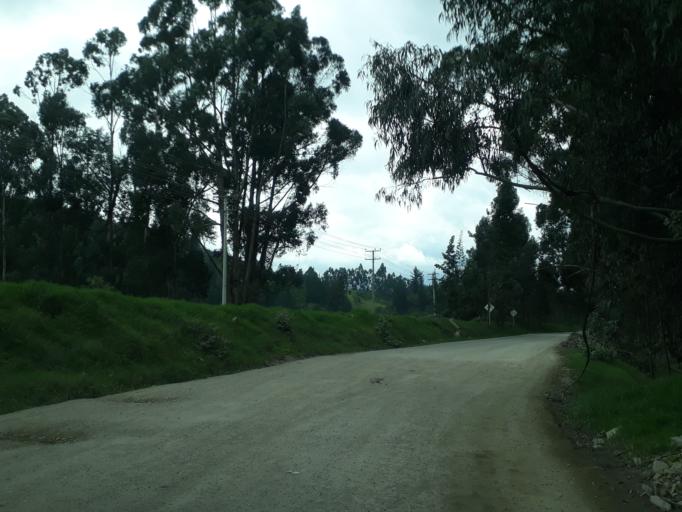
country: CO
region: Cundinamarca
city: Lenguazaque
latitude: 5.3265
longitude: -73.7544
